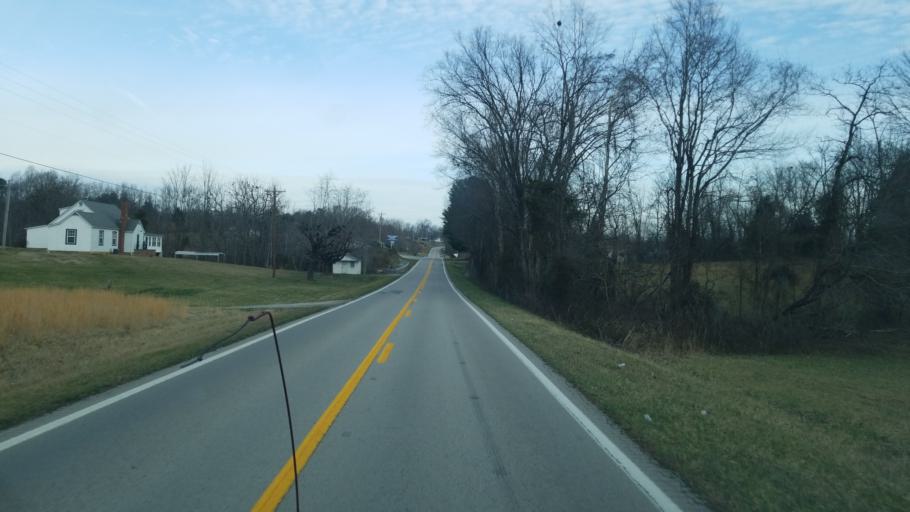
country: US
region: Kentucky
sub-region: Clinton County
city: Albany
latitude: 36.7988
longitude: -85.1812
